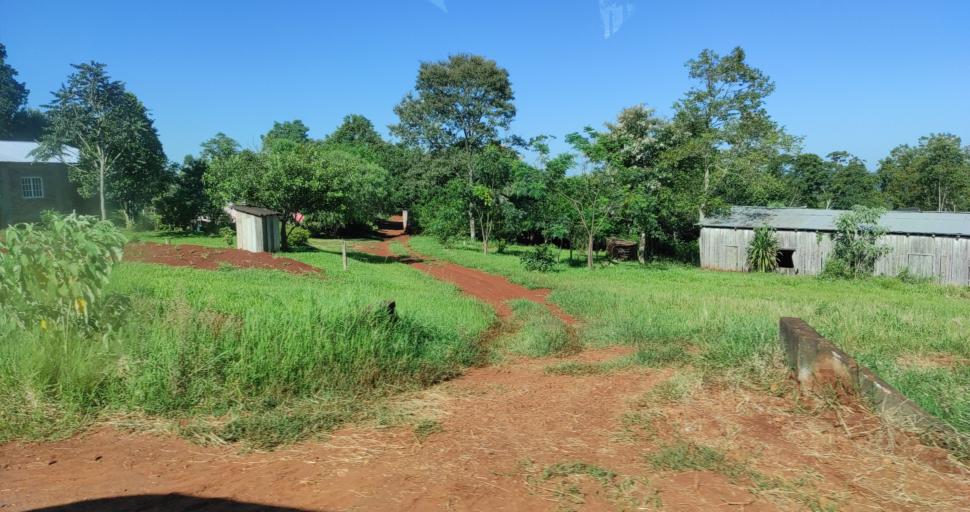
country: AR
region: Misiones
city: El Soberbio
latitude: -27.1873
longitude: -54.1062
